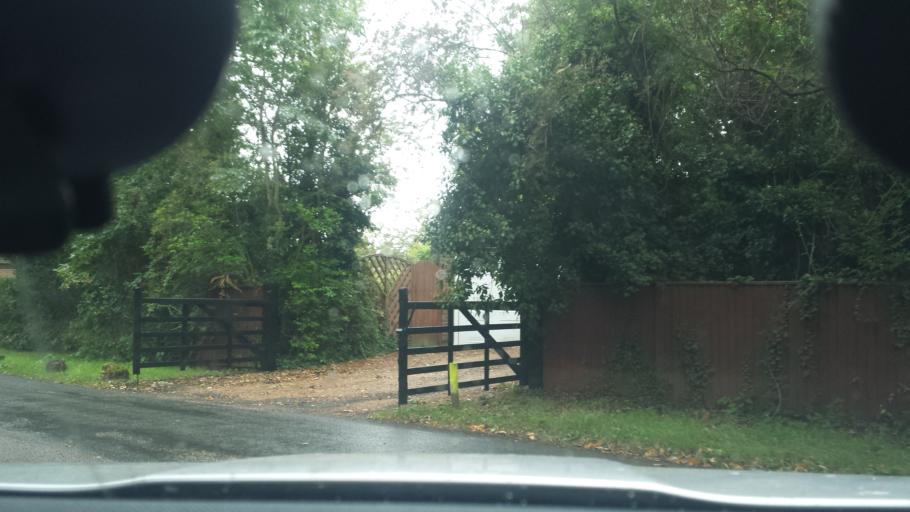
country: GB
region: England
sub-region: Kent
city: Staplehurst
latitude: 51.1731
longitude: 0.5459
